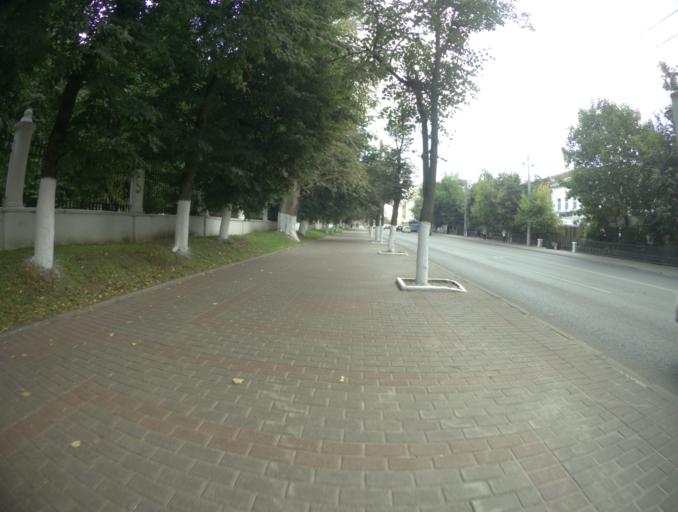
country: RU
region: Vladimir
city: Vladimir
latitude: 56.1303
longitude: 40.4099
